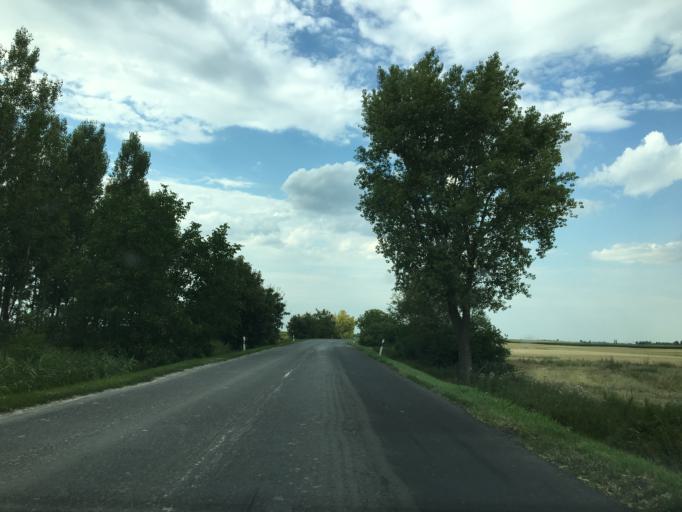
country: HU
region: Bacs-Kiskun
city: Dusnok
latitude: 46.3962
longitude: 18.9427
